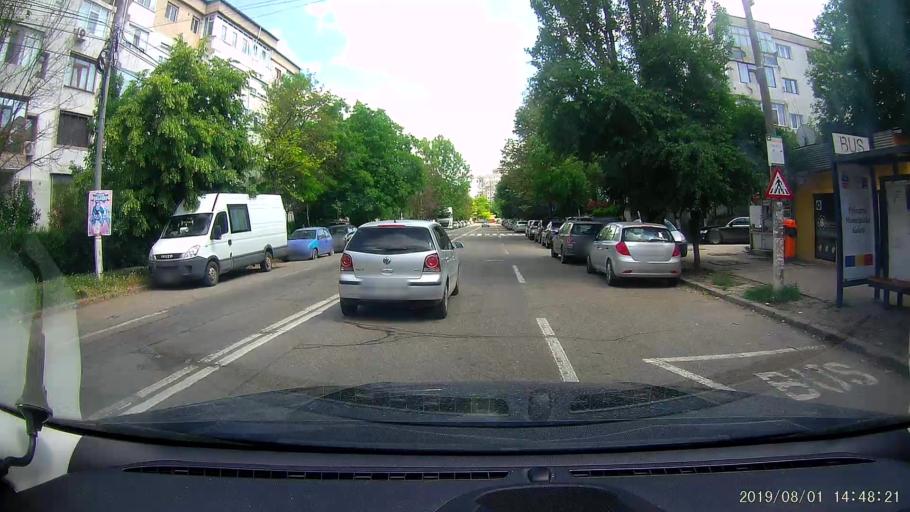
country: RO
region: Galati
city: Galati
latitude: 45.4112
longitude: 28.0084
